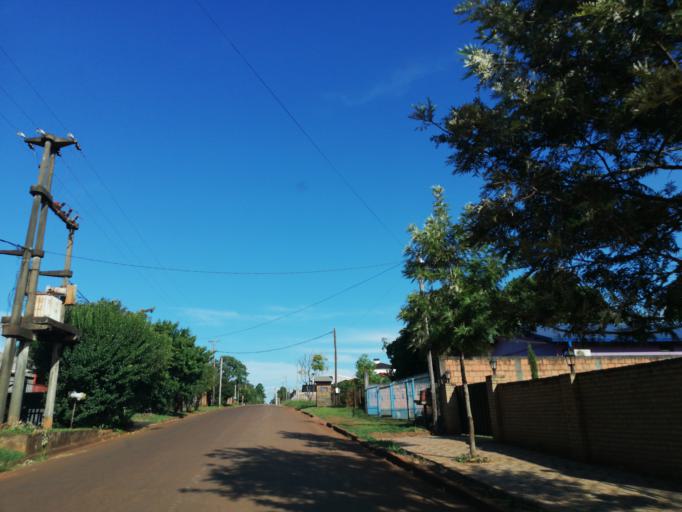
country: AR
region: Misiones
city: Dos de Mayo
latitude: -26.9941
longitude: -54.4944
